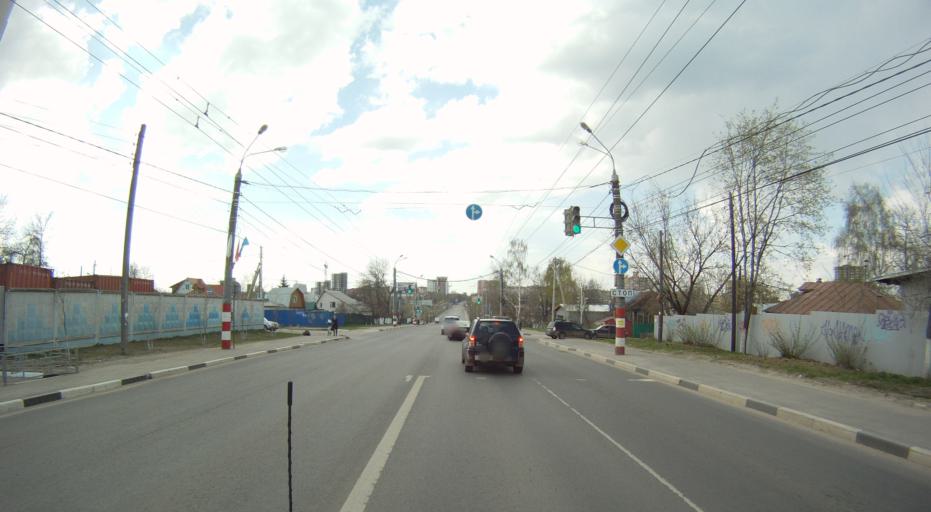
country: RU
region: Nizjnij Novgorod
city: Nizhniy Novgorod
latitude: 56.3027
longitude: 44.0294
